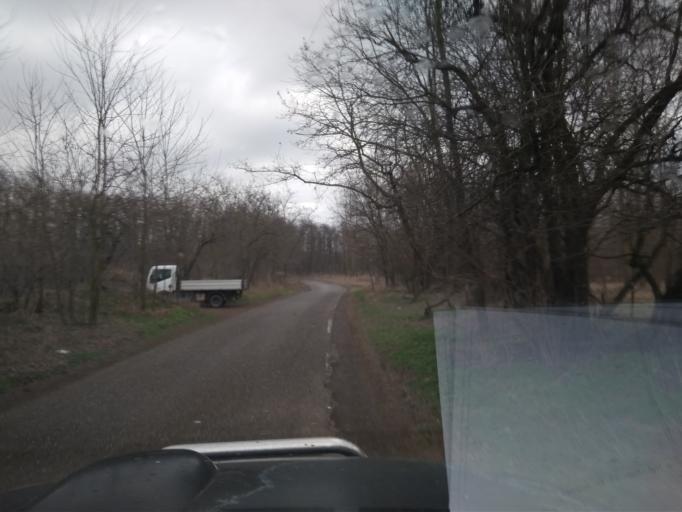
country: HU
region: Szabolcs-Szatmar-Bereg
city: Nyirpazony
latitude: 48.0256
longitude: 21.7958
